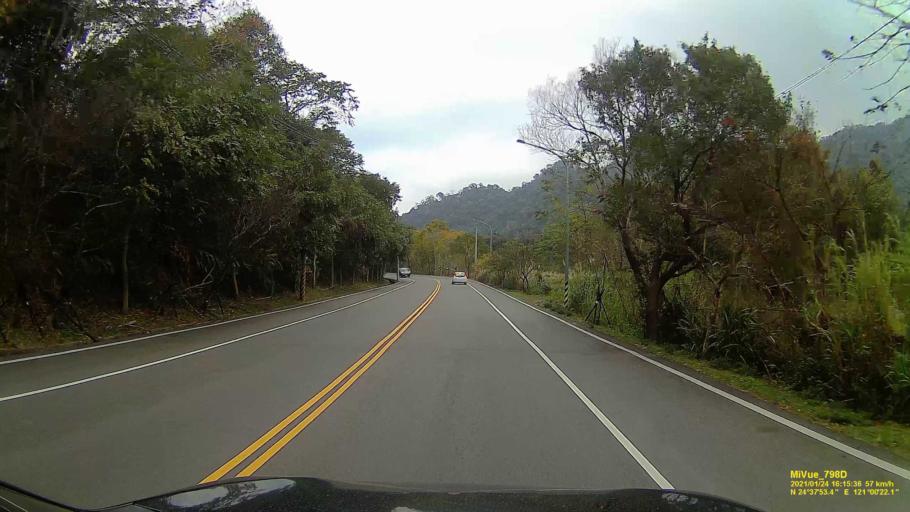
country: TW
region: Taiwan
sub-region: Hsinchu
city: Hsinchu
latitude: 24.6320
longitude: 121.0061
